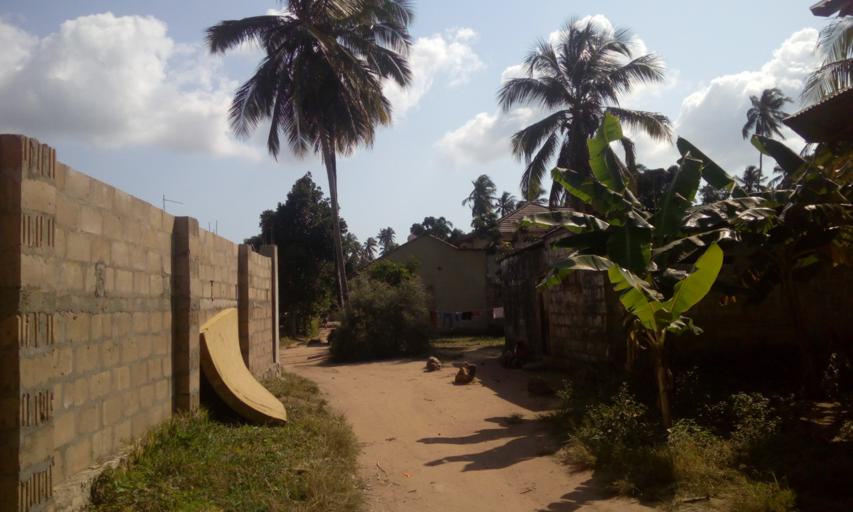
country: TZ
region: Zanzibar Central/South
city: Koani
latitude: -6.1998
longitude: 39.2639
